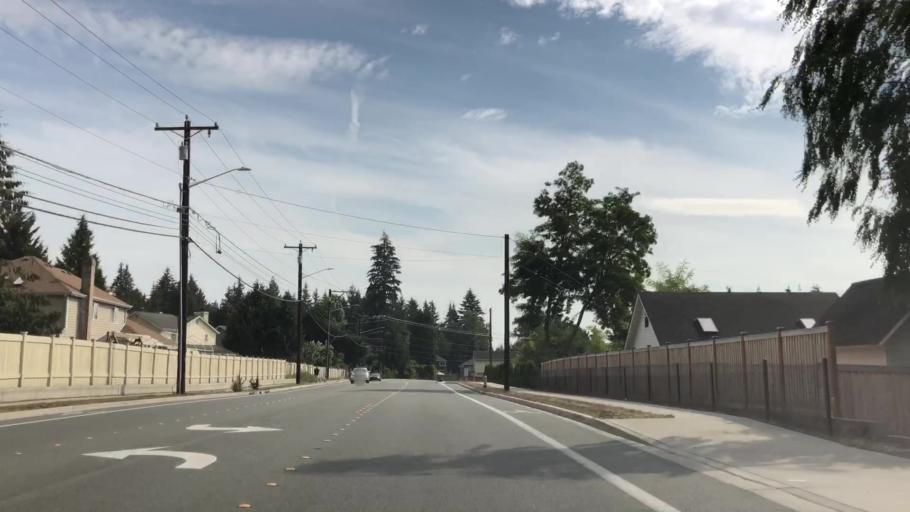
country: US
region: Washington
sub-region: Snohomish County
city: Martha Lake
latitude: 47.8405
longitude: -122.2357
